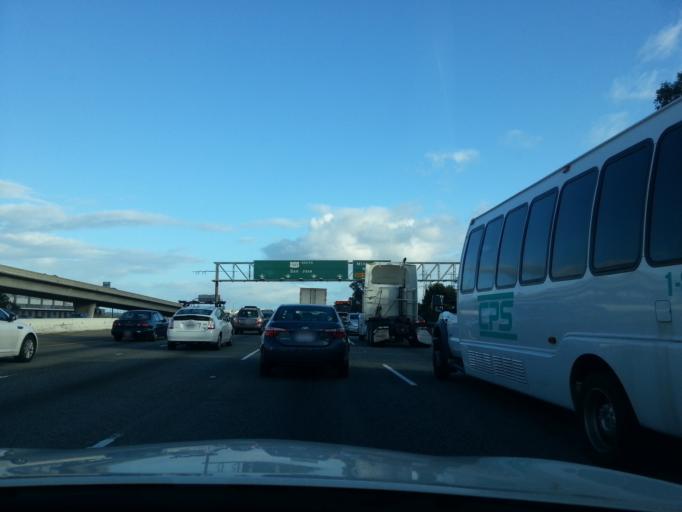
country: US
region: California
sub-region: San Mateo County
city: Millbrae
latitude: 37.6094
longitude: -122.3911
